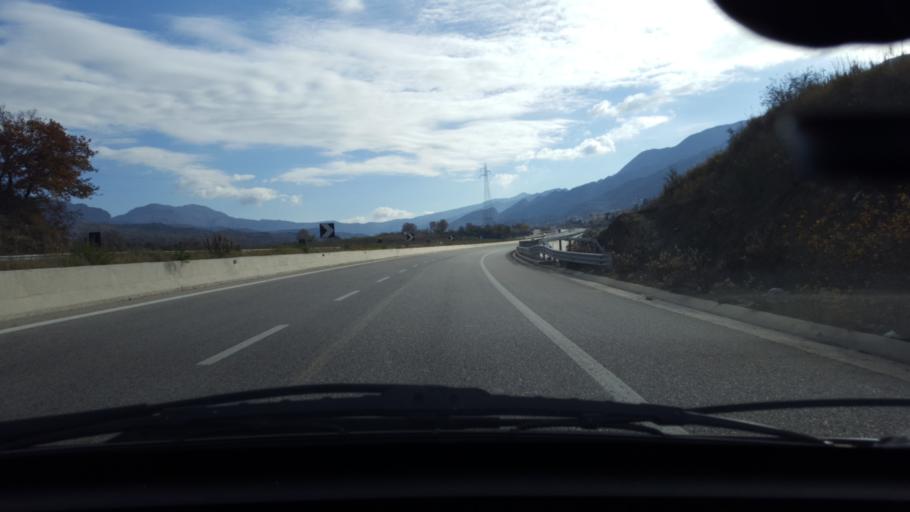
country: AL
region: Tirane
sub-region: Rrethi i Tiranes
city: Berzhite
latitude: 41.2590
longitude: 19.8894
